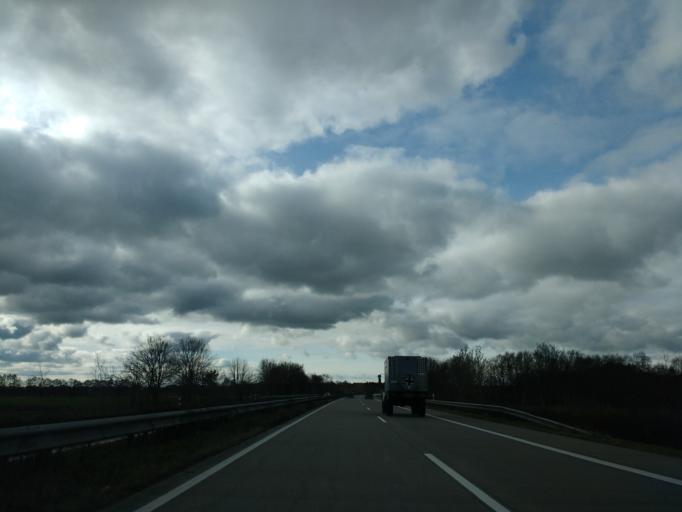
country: DE
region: Lower Saxony
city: Midlum
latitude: 53.7677
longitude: 8.6978
